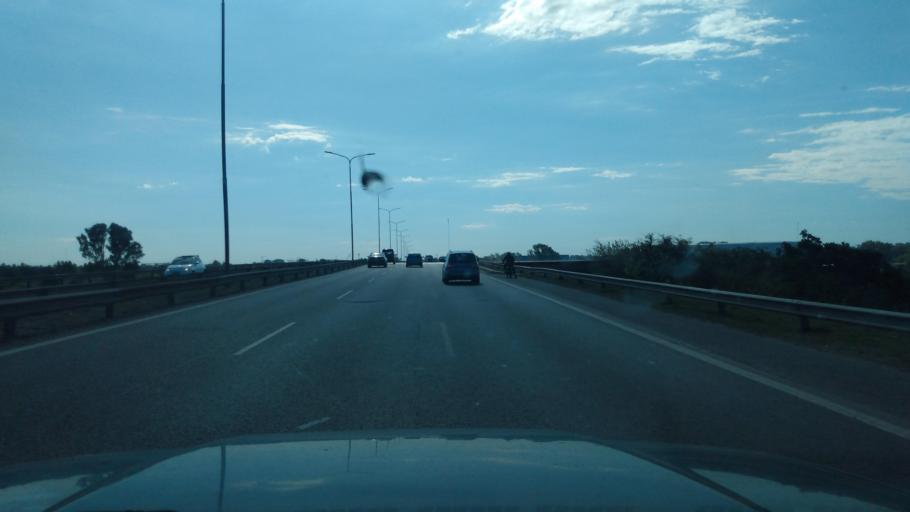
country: AR
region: Buenos Aires
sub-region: Partido de Tigre
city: Tigre
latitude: -34.5112
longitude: -58.5909
